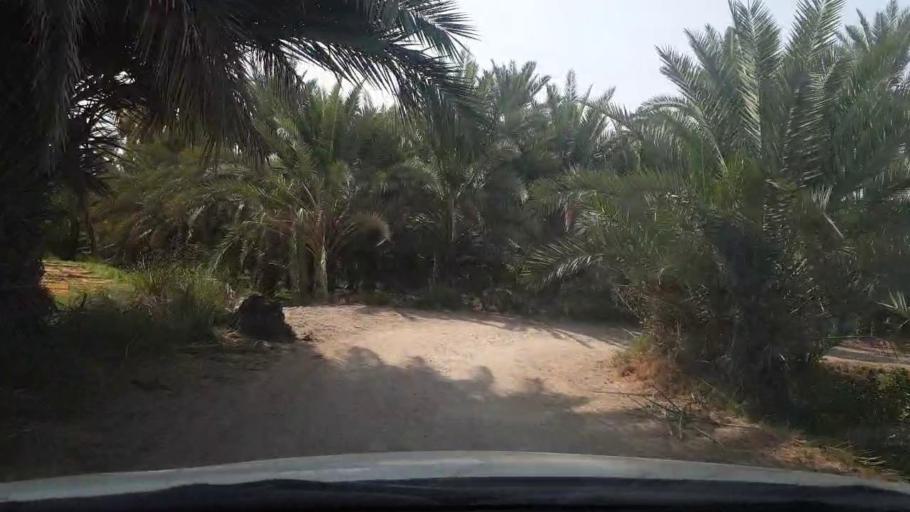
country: PK
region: Sindh
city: Rohri
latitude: 27.5895
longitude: 68.8551
